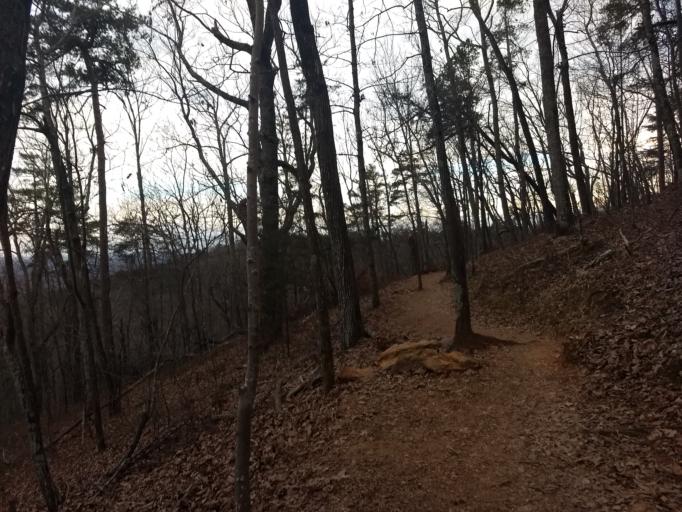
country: US
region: South Carolina
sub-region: Greenville County
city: Travelers Rest
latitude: 34.9451
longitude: -82.3902
